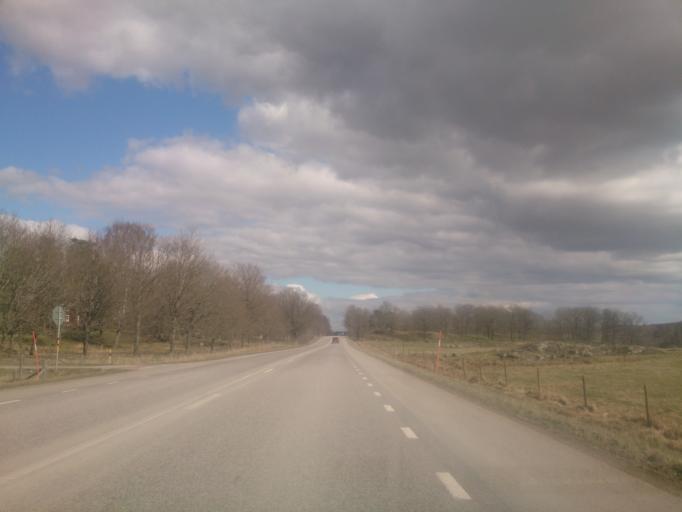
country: SE
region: OEstergoetland
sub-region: Norrkopings Kommun
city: Norrkoping
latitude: 58.5688
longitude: 16.0873
